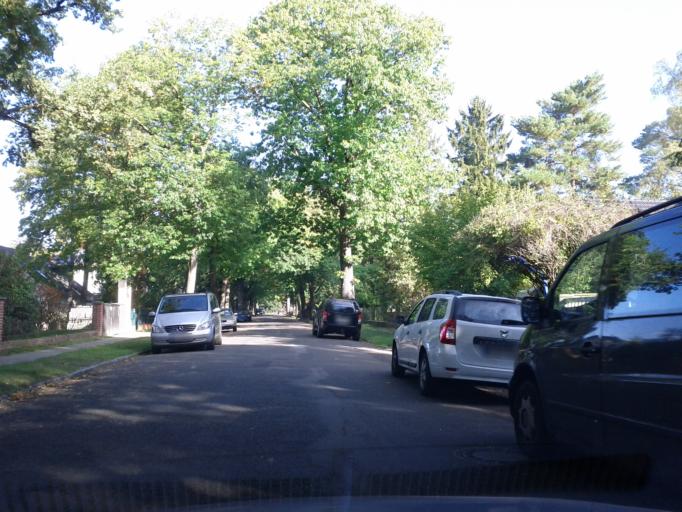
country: DE
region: Brandenburg
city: Schoneiche
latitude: 52.4677
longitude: 13.6916
